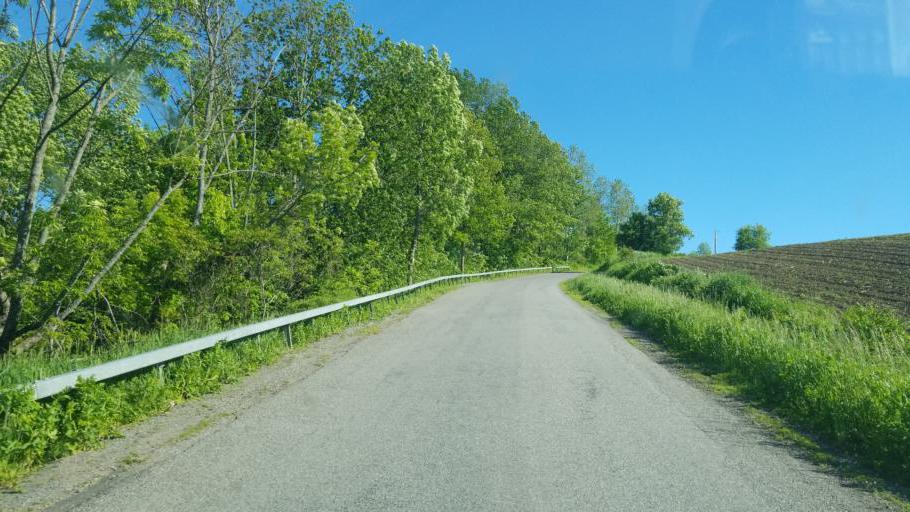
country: US
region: New York
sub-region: Herkimer County
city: Little Falls
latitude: 42.9961
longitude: -74.7793
